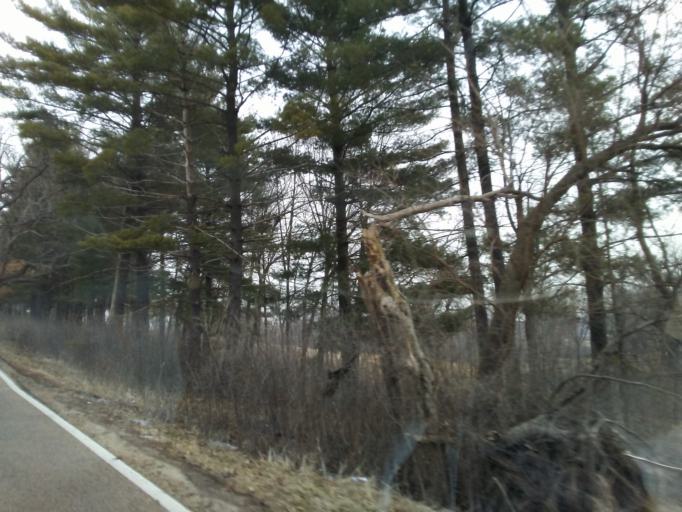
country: US
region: Wisconsin
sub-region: Dane County
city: Middleton
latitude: 43.1126
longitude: -89.4914
